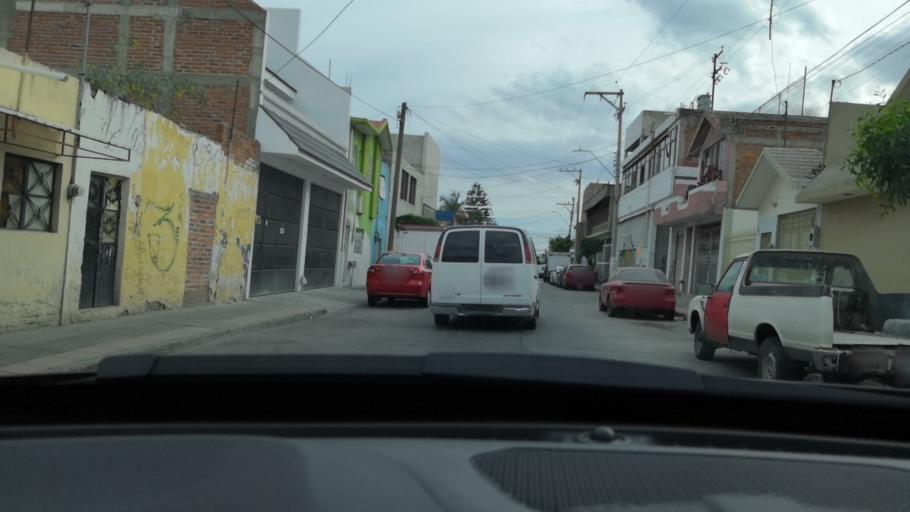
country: MX
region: Guanajuato
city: Leon
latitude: 21.1294
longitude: -101.7061
